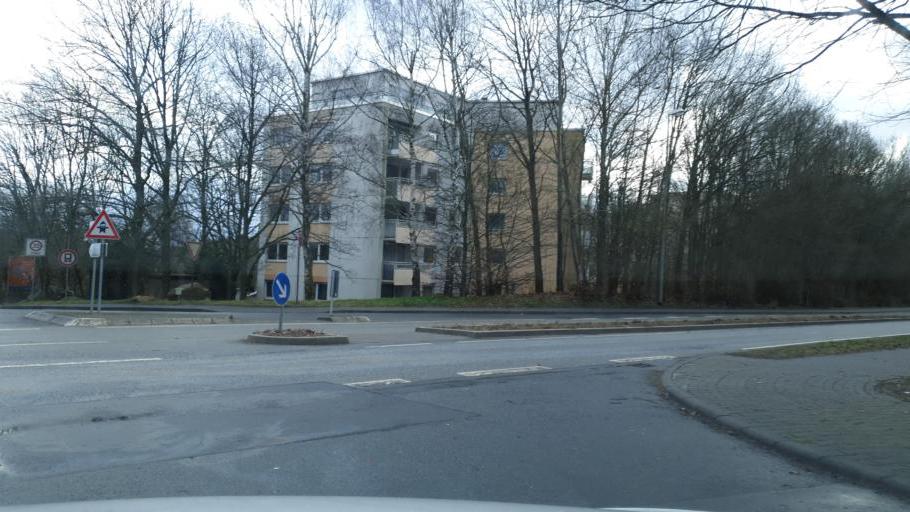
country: DE
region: Hesse
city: Eppstein
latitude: 50.1348
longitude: 8.3555
